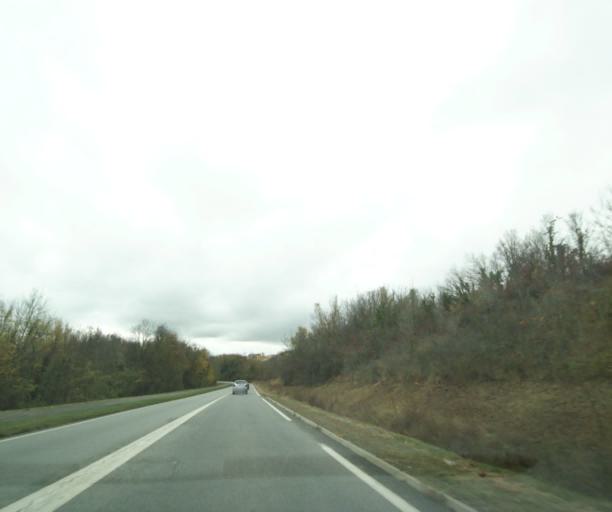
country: FR
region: Auvergne
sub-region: Departement du Puy-de-Dome
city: Cournon-d'Auvergne
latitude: 45.7511
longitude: 3.2121
